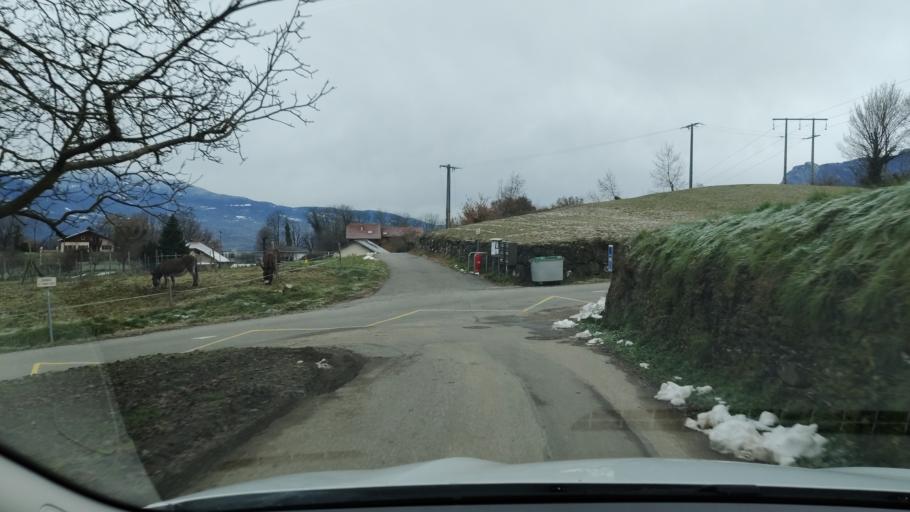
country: FR
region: Rhone-Alpes
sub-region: Departement de la Savoie
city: Montmelian
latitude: 45.4555
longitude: 6.0633
